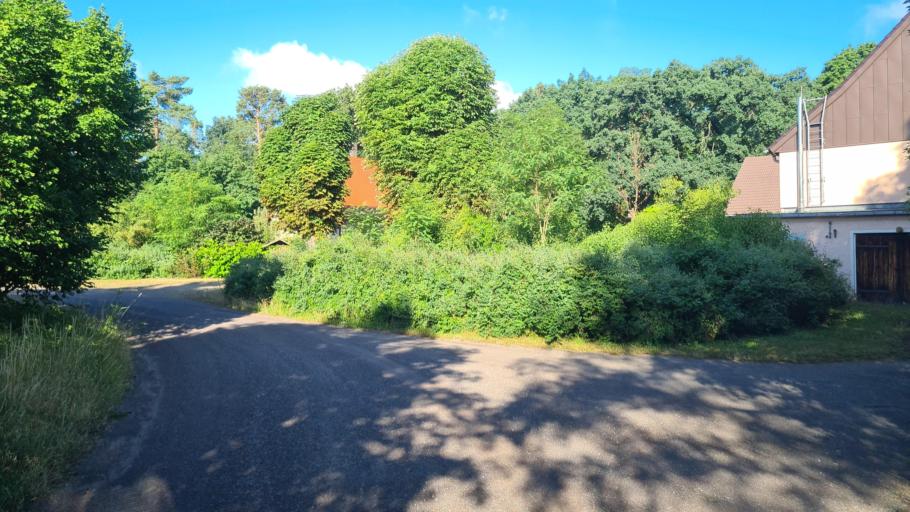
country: DE
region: Saxony
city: Beilrode
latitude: 51.6422
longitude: 13.0911
